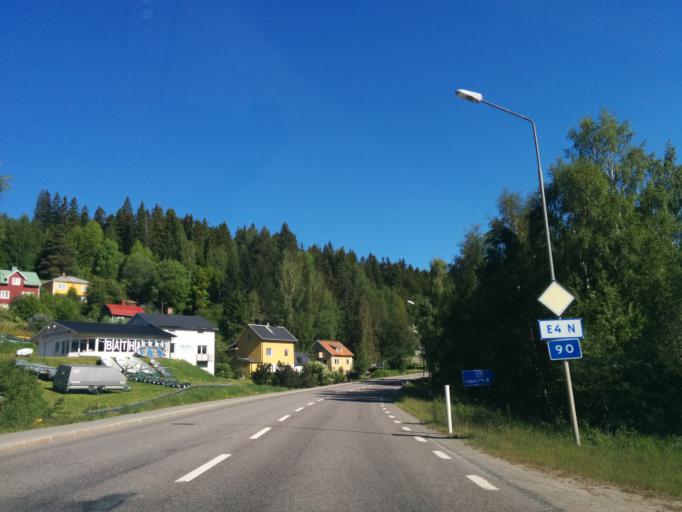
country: SE
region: Vaesternorrland
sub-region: Kramfors Kommun
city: Kramfors
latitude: 62.9364
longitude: 17.7702
